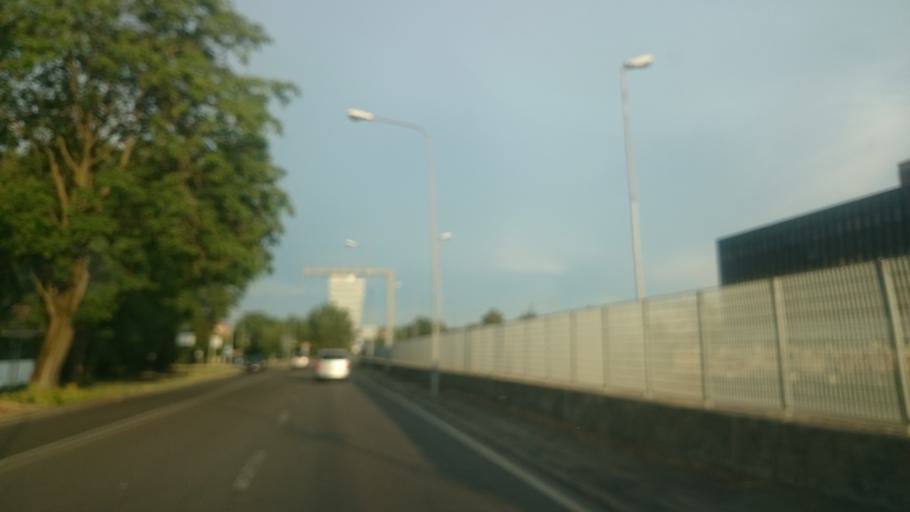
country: IT
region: Emilia-Romagna
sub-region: Provincia di Reggio Emilia
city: Reggio nell'Emilia
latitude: 44.7099
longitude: 10.6345
